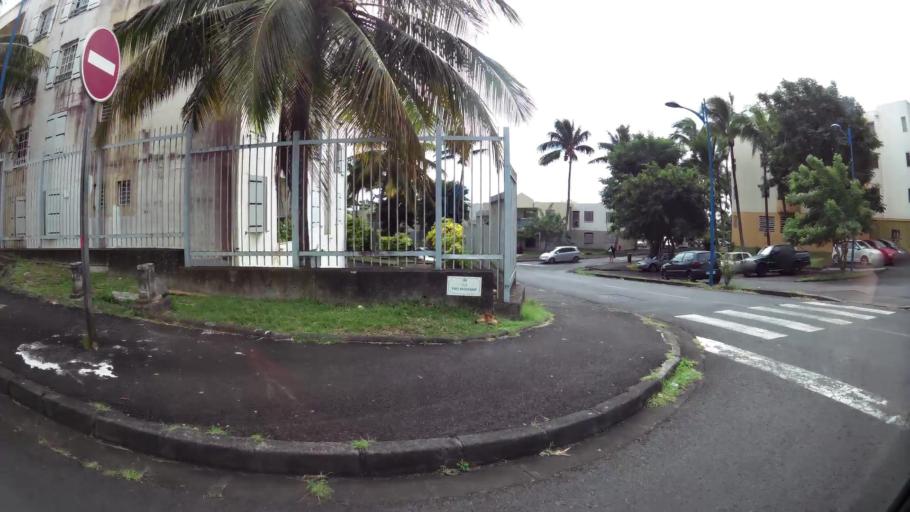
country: RE
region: Reunion
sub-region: Reunion
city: Sainte-Marie
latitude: -20.8984
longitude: 55.5560
